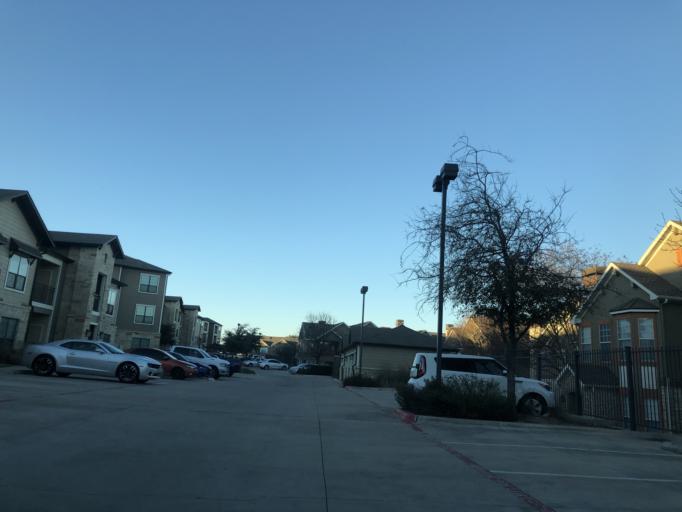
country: US
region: Texas
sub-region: Travis County
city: Windemere
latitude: 30.4857
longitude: -97.6539
